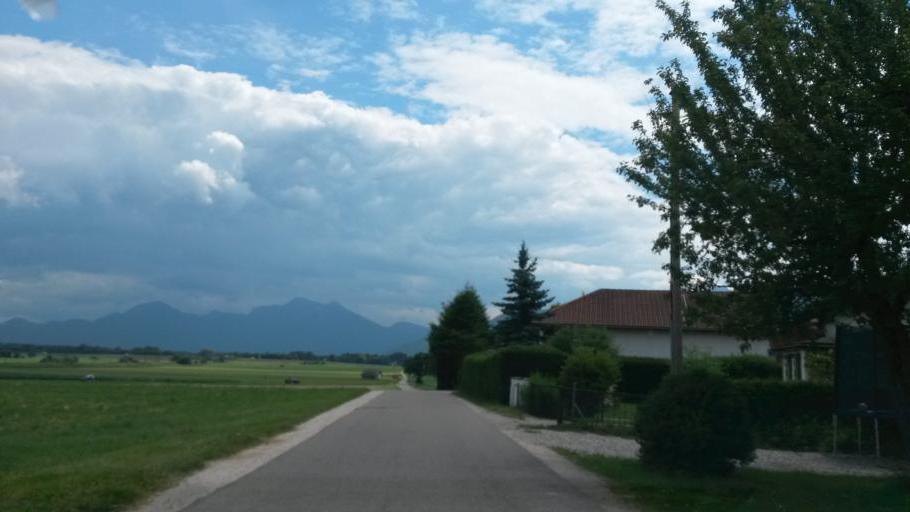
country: DE
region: Bavaria
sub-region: Upper Bavaria
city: Bernau am Chiemsee
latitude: 47.8254
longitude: 12.3583
